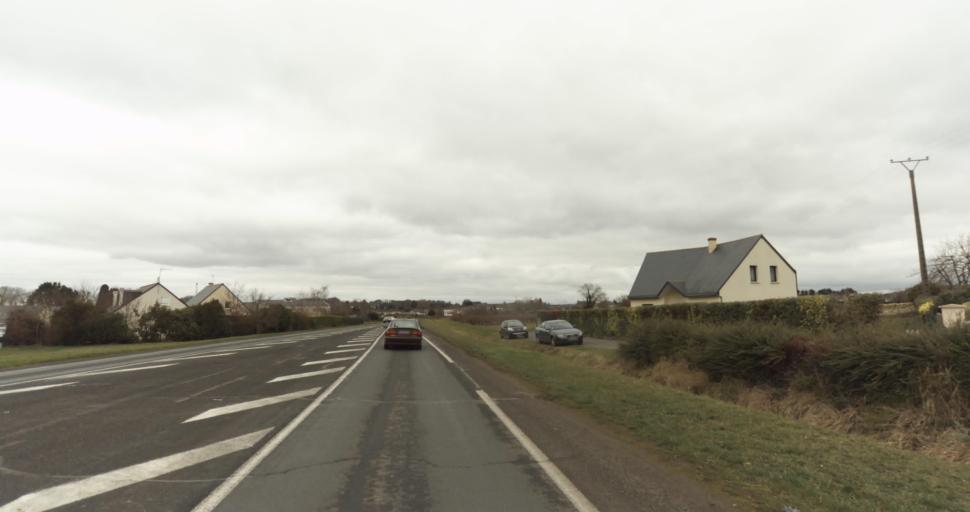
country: FR
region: Pays de la Loire
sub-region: Departement de Maine-et-Loire
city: Varrains
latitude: 47.2180
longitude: -0.0596
